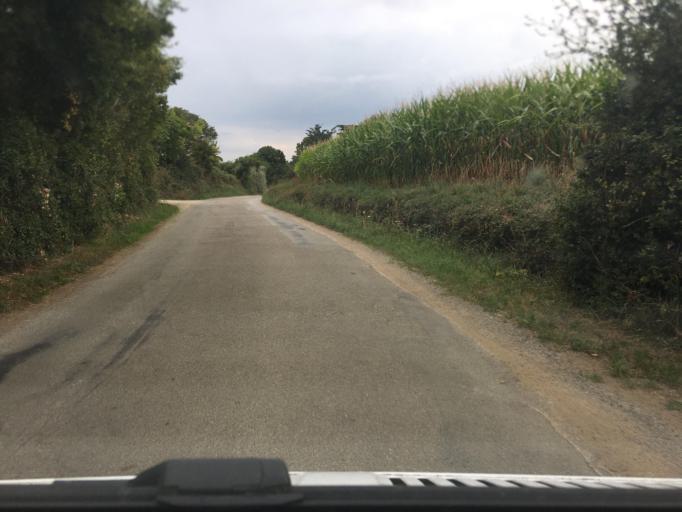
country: FR
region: Brittany
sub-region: Departement du Finistere
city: Beuzec-Cap-Sizun
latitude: 48.0818
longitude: -4.4768
